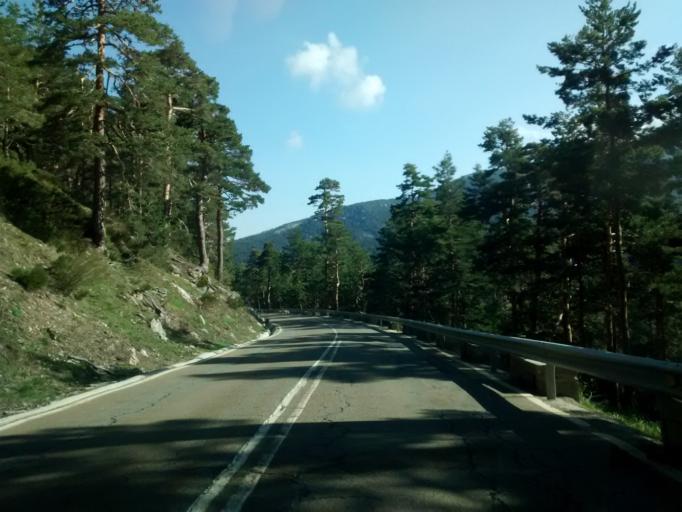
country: ES
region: Madrid
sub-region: Provincia de Madrid
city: Navacerrada
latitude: 40.8075
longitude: -4.0057
